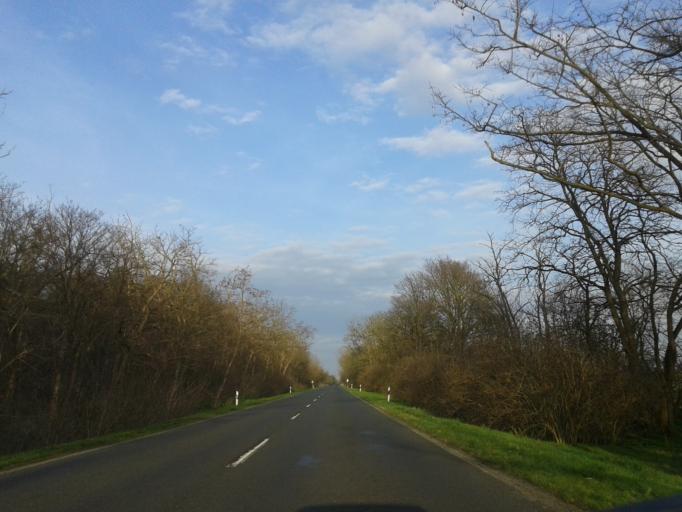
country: HU
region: Gyor-Moson-Sopron
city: Bony
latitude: 47.7350
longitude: 17.9115
